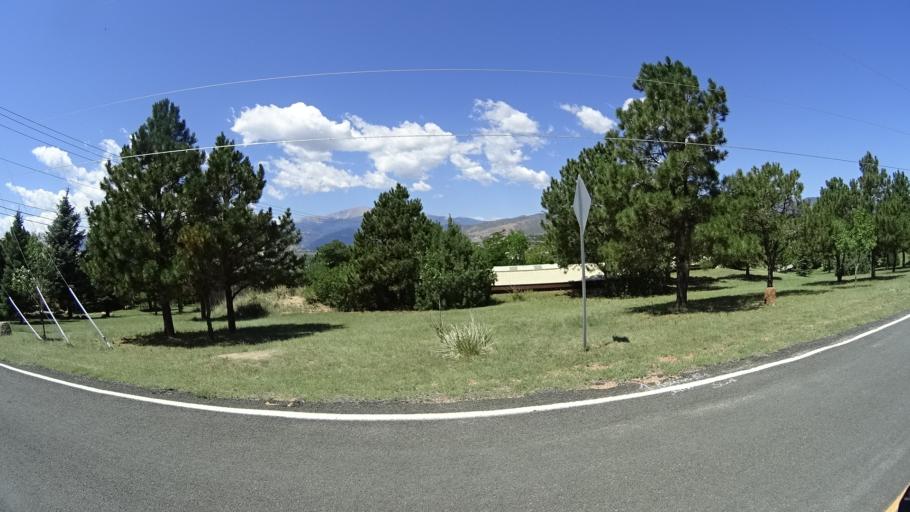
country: US
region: Colorado
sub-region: El Paso County
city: Colorado Springs
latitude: 38.9023
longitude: -104.8090
